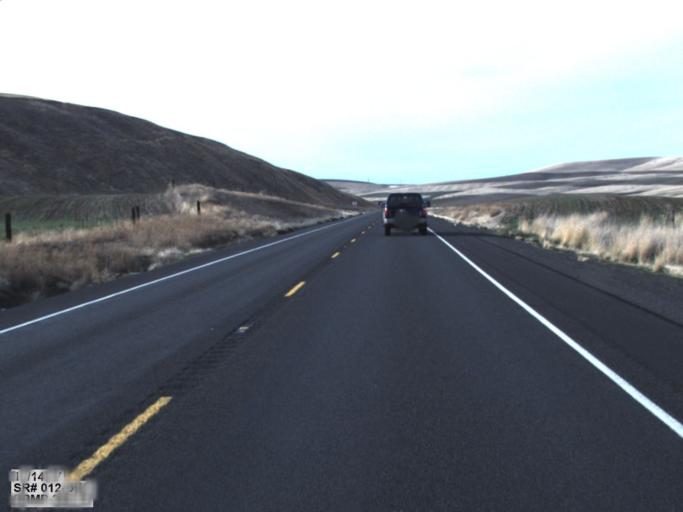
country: US
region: Washington
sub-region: Columbia County
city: Dayton
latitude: 46.5380
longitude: -117.8588
